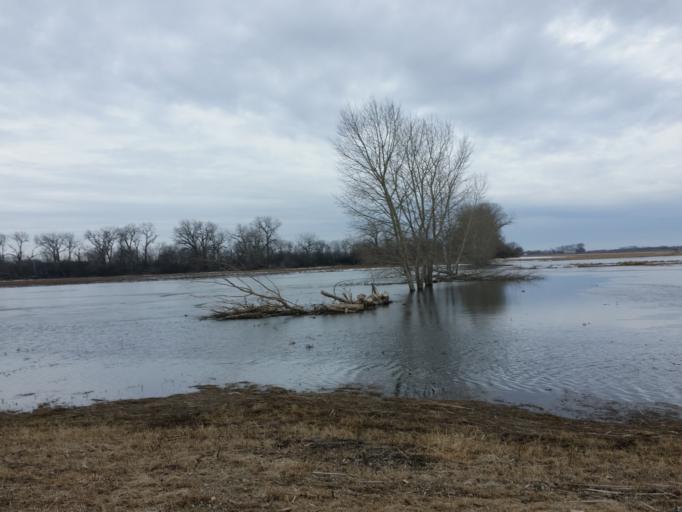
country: US
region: North Dakota
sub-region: Walsh County
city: Grafton
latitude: 48.4054
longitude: -97.4703
